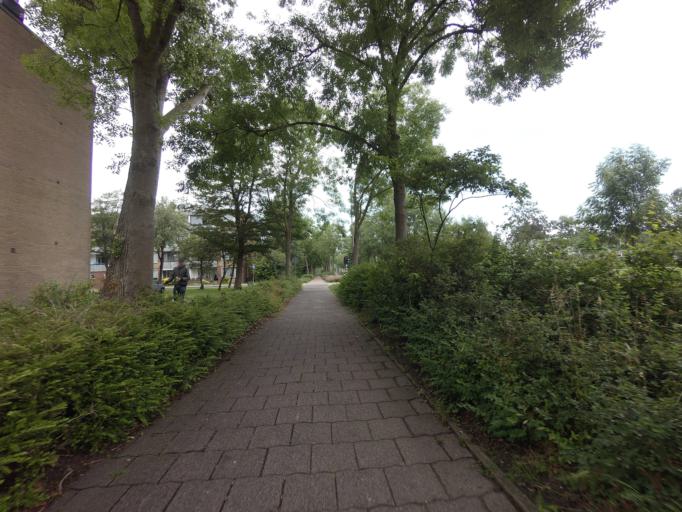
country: NL
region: North Holland
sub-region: Gemeente Purmerend
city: Purmerend
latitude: 52.5138
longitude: 4.9648
